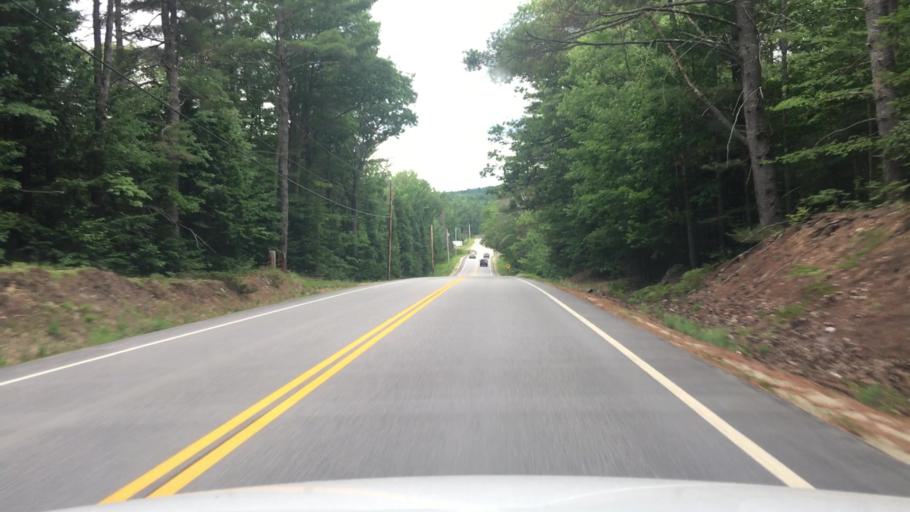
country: US
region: Maine
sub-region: Oxford County
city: Hartford
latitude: 44.3585
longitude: -70.3637
